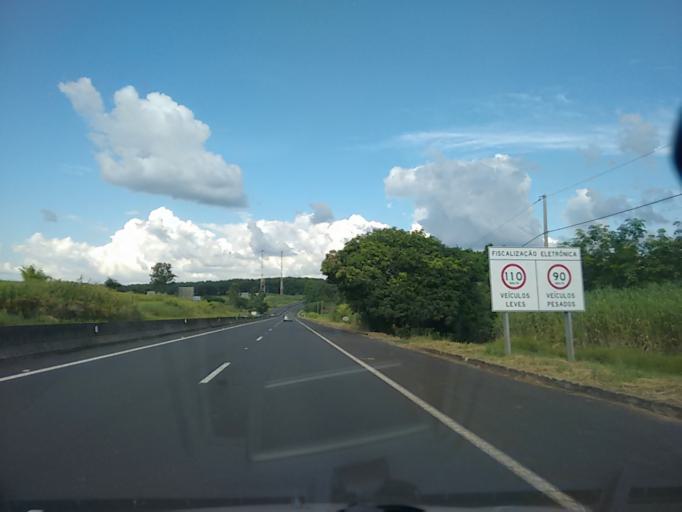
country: BR
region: Sao Paulo
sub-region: Marilia
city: Marilia
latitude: -22.2162
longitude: -49.8513
